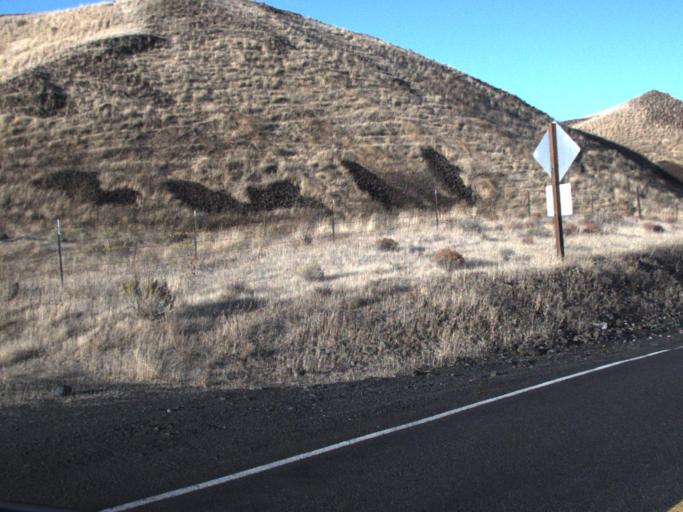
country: US
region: Washington
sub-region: Walla Walla County
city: Waitsburg
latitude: 46.6065
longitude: -118.2240
